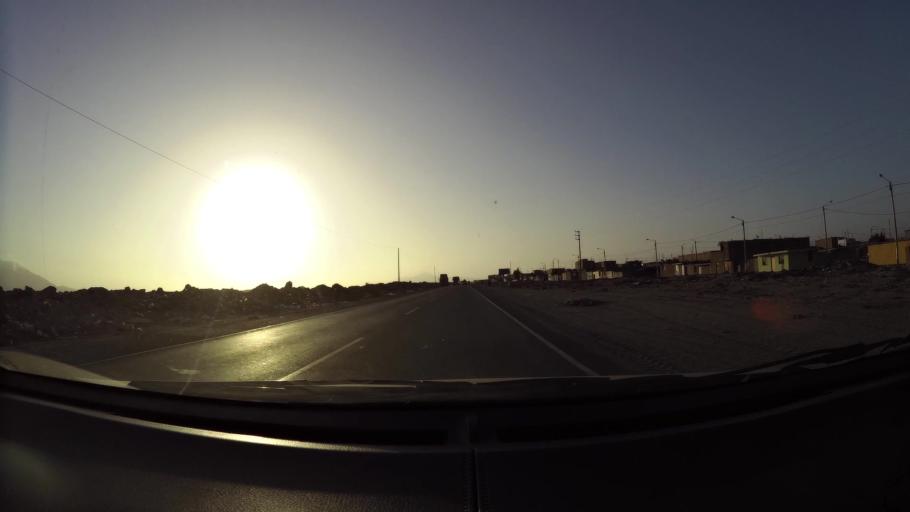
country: PE
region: Ancash
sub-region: Provincia de Santa
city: Buenos Aires
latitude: -9.1512
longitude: -78.5066
